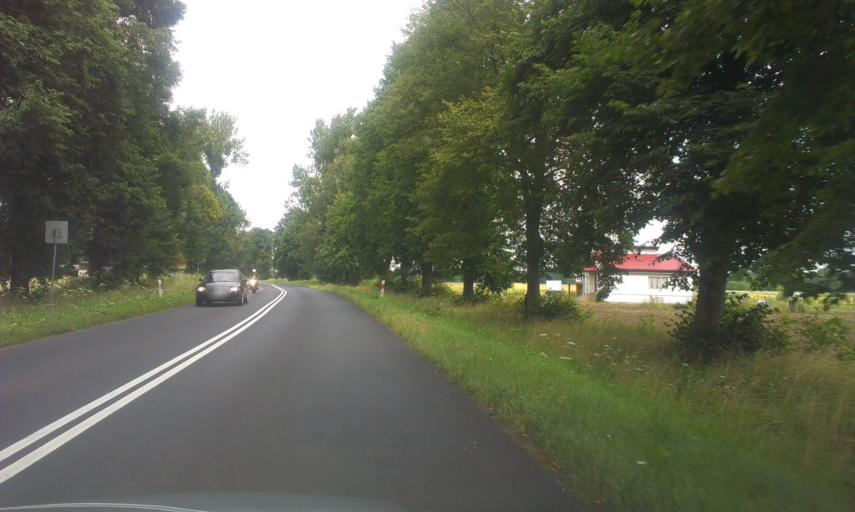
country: PL
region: West Pomeranian Voivodeship
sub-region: Powiat swidwinski
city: Rabino
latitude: 53.9035
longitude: 16.0686
